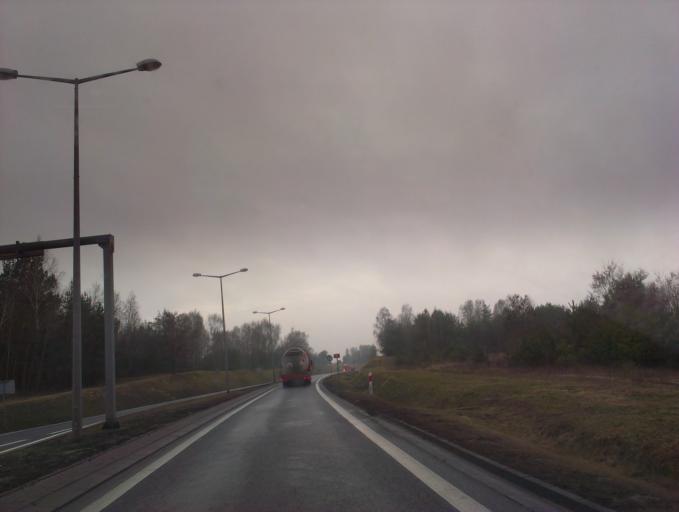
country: PL
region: Greater Poland Voivodeship
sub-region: Powiat pilski
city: Pila
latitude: 53.1490
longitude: 16.7881
